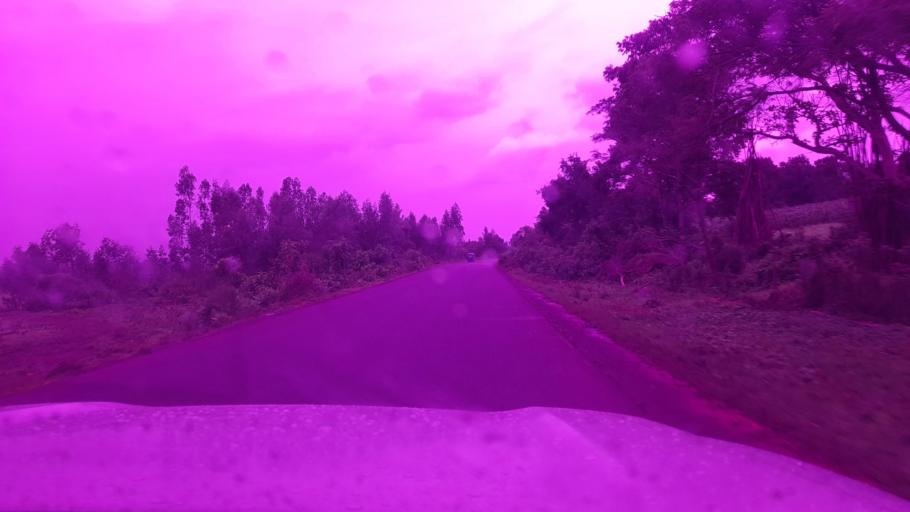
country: ET
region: Oromiya
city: Jima
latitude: 7.7089
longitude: 37.0364
